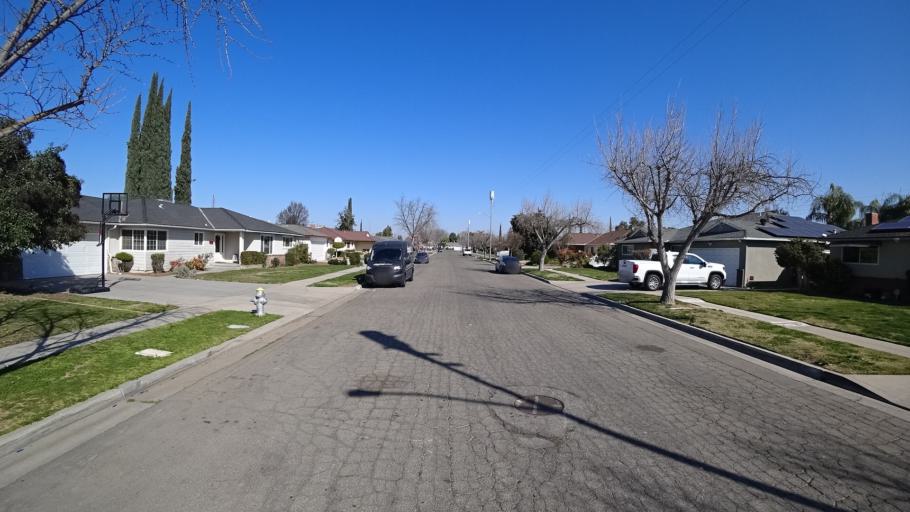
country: US
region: California
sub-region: Fresno County
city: Clovis
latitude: 36.8286
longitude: -119.7695
